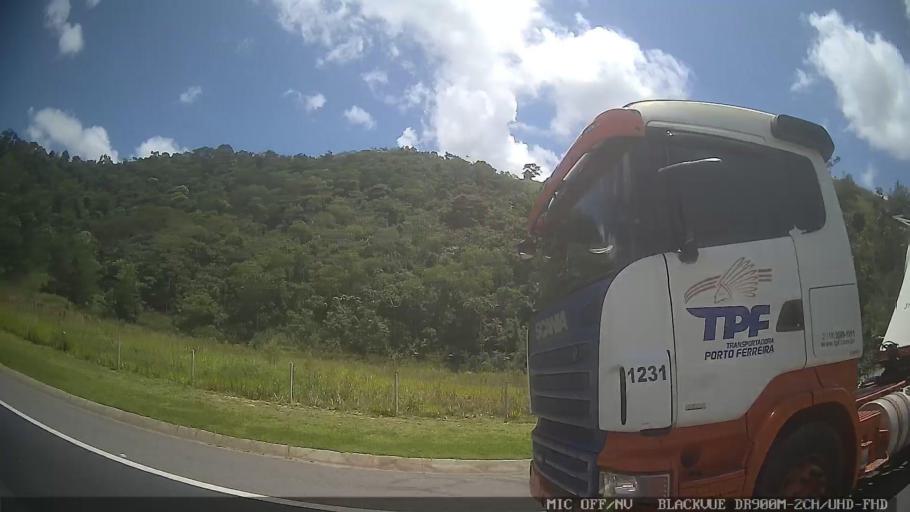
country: BR
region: Sao Paulo
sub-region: Caraguatatuba
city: Caraguatatuba
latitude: -23.4759
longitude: -45.5856
